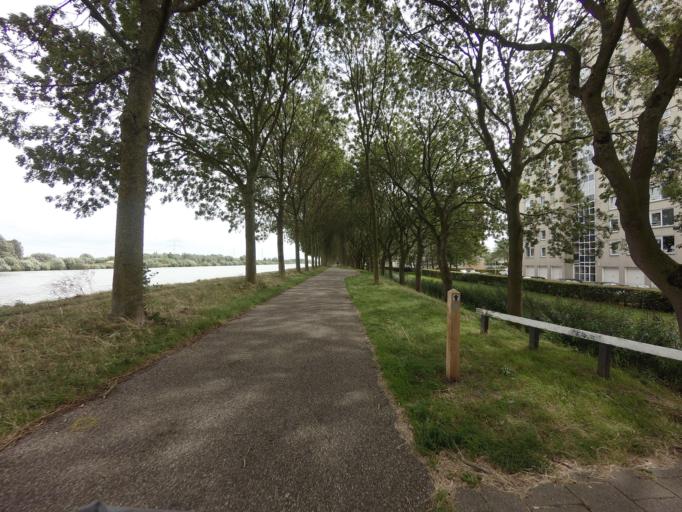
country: NL
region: North Holland
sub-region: Gemeente Diemen
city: Diemen
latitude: 52.3496
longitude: 4.9833
